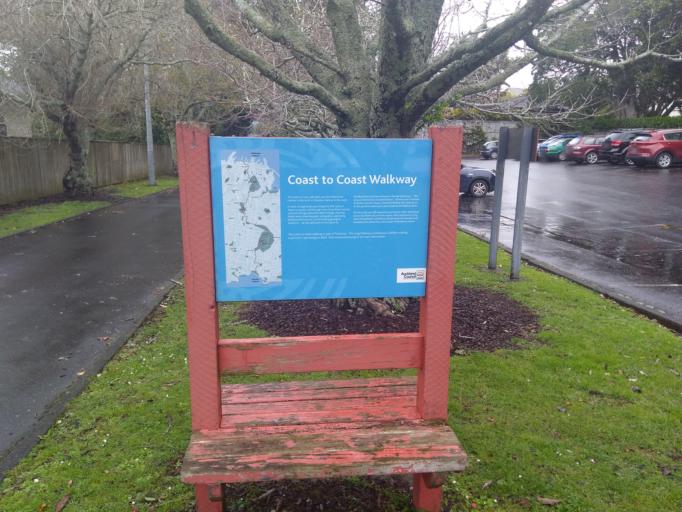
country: NZ
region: Auckland
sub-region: Auckland
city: Auckland
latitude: -36.8824
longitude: 174.7688
